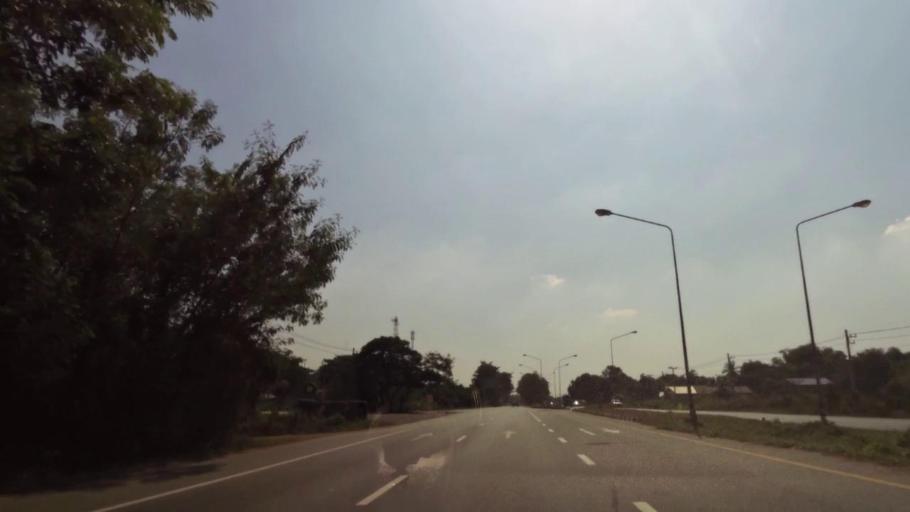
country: TH
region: Phichit
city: Bueng Na Rang
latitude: 16.1942
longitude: 100.1285
